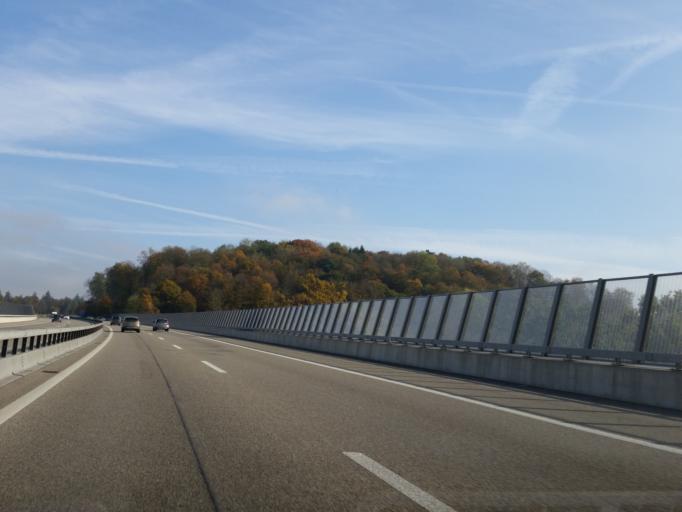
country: CH
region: Aargau
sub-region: Bezirk Lenzburg
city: Niederlenz
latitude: 47.3956
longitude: 8.1775
